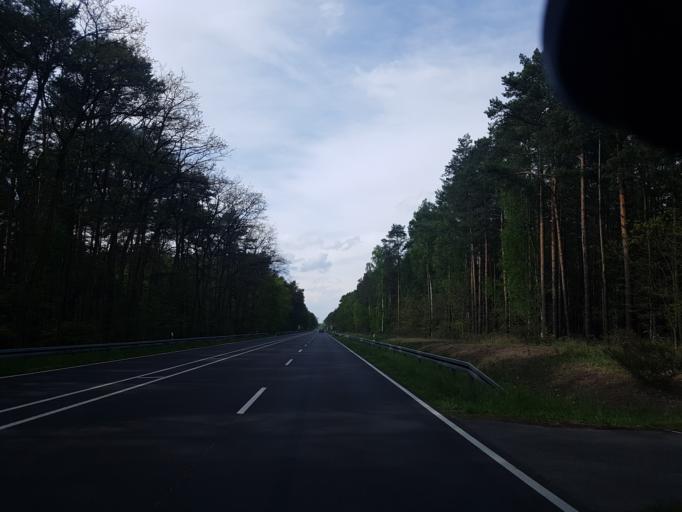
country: DE
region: Saxony
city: Gross Duben
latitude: 51.6535
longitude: 14.5350
